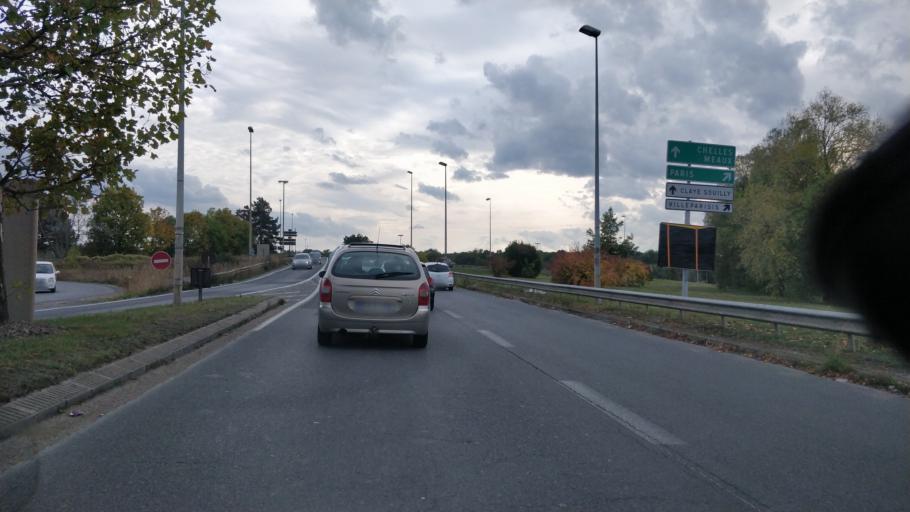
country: FR
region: Ile-de-France
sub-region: Departement de Seine-et-Marne
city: Claye-Souilly
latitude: 48.9455
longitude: 2.6674
